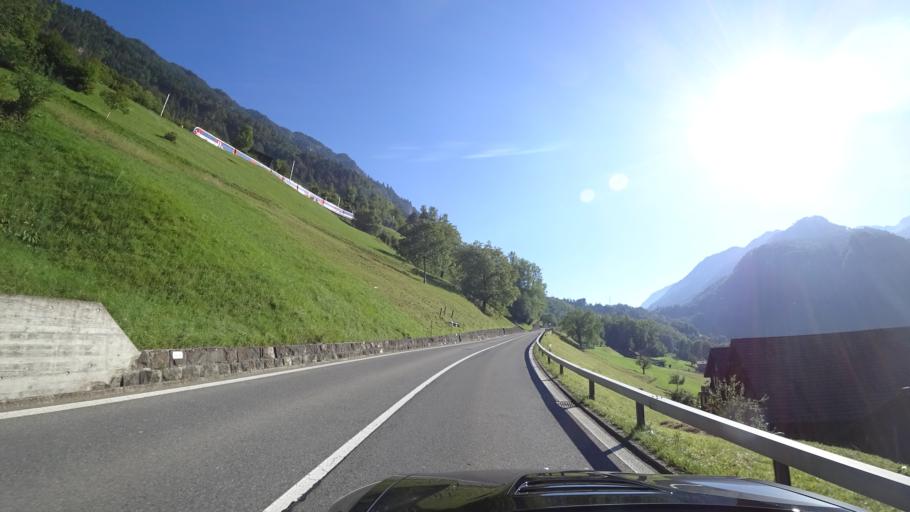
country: CH
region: Obwalden
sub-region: Obwalden
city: Giswil
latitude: 46.8286
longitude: 8.1853
